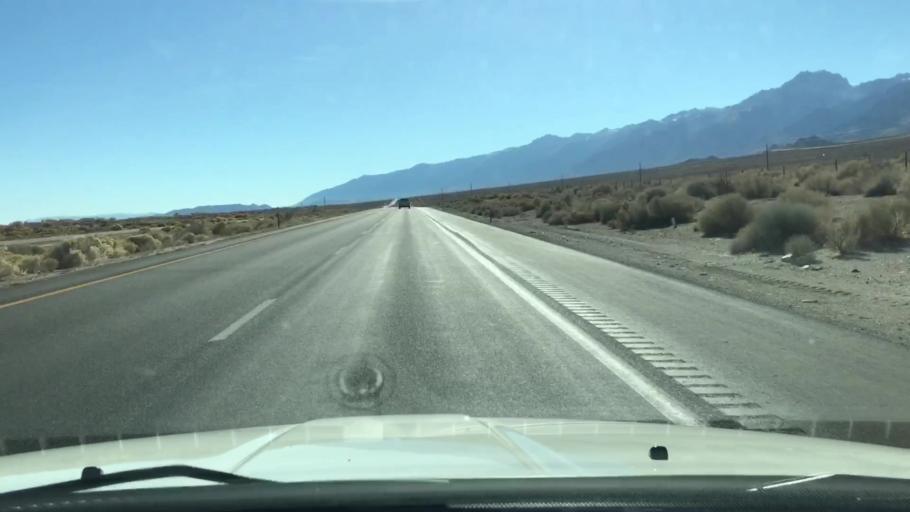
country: US
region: California
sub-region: Inyo County
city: Big Pine
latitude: 36.8811
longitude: -118.2399
